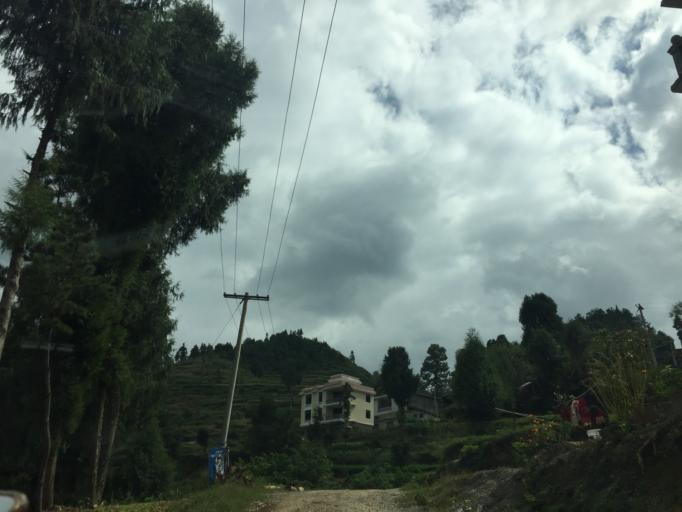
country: CN
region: Guizhou Sheng
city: Xujiaba
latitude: 27.9645
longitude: 108.1555
